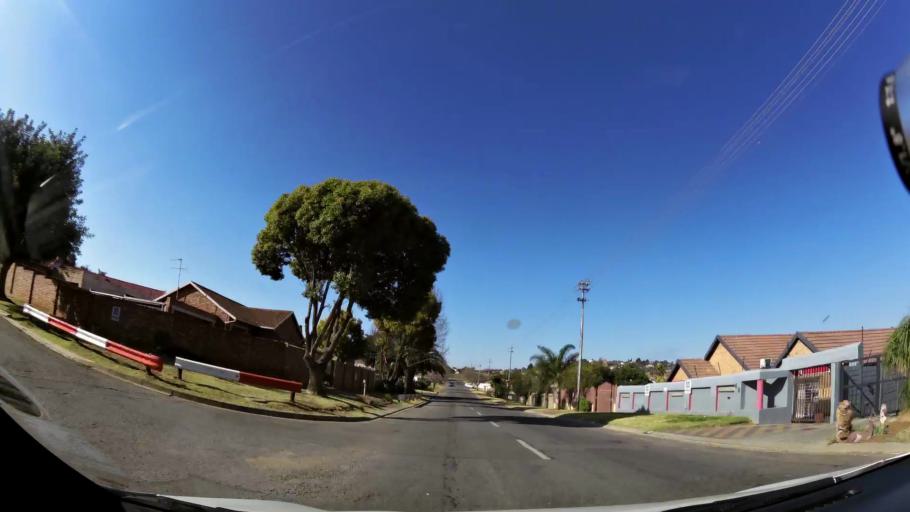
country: ZA
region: Gauteng
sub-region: City of Johannesburg Metropolitan Municipality
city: Johannesburg
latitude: -26.2777
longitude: 28.0311
